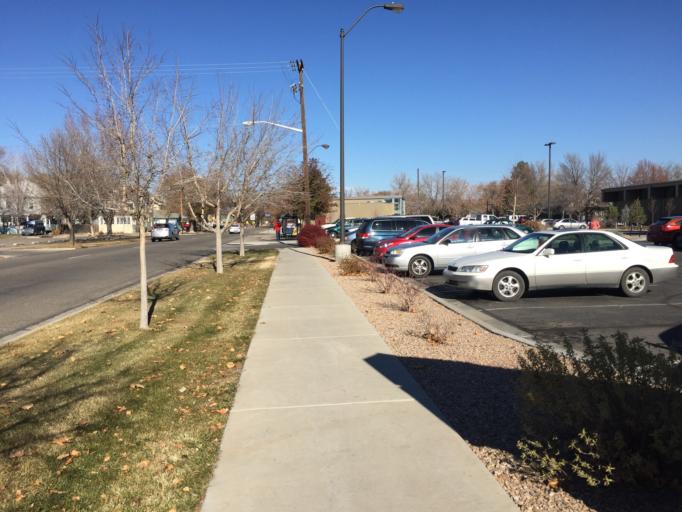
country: US
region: Colorado
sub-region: Mesa County
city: Grand Junction
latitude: 39.0706
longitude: -108.5643
